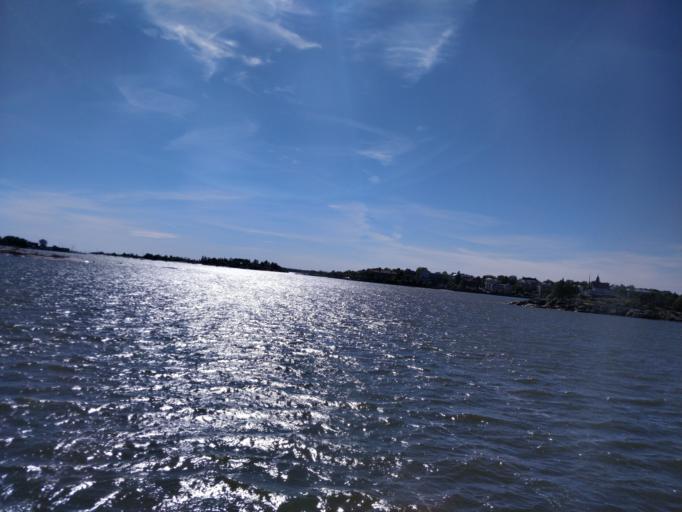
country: FI
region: Uusimaa
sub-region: Helsinki
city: Helsinki
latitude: 60.1597
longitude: 24.9777
